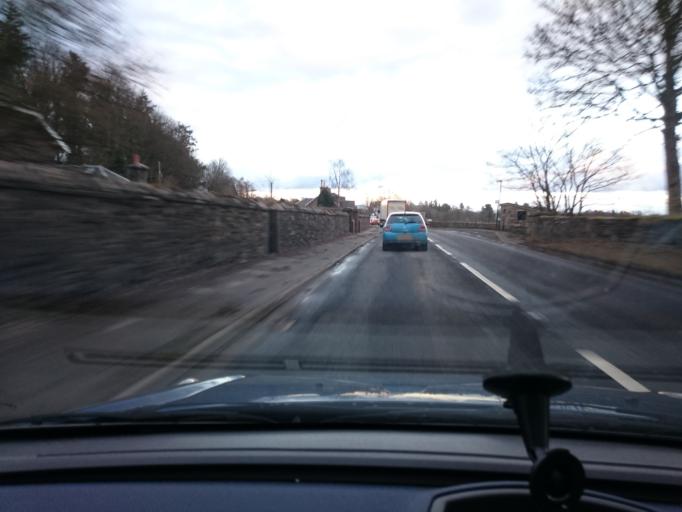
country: GB
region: Scotland
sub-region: Stirling
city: Doune
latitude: 56.2011
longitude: -4.0813
